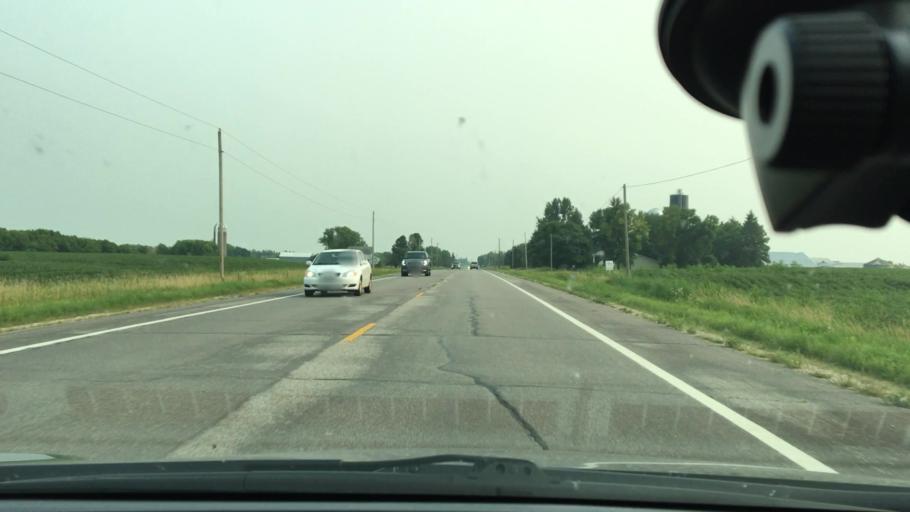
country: US
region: Minnesota
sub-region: Wright County
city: Albertville
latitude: 45.2734
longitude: -93.6637
